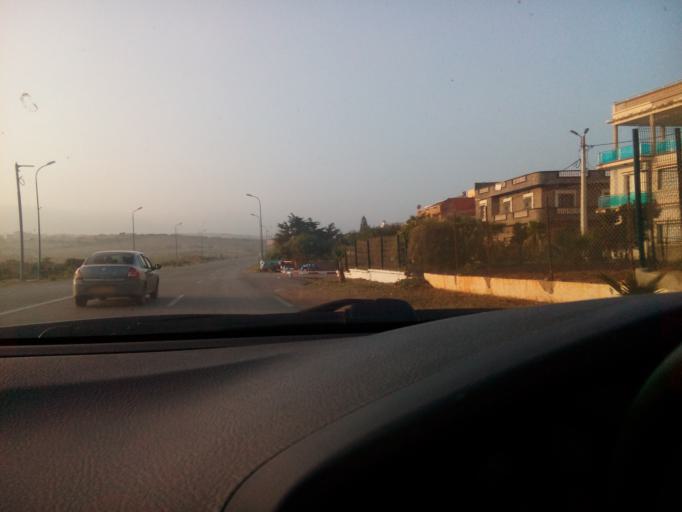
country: DZ
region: Oran
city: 'Ain el Turk
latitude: 35.7299
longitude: -0.8422
